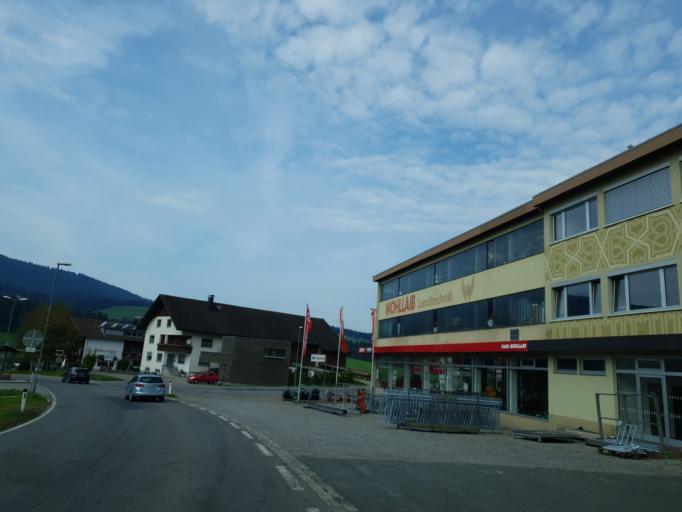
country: AT
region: Vorarlberg
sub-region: Politischer Bezirk Bregenz
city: Doren
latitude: 47.5140
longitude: 9.8668
